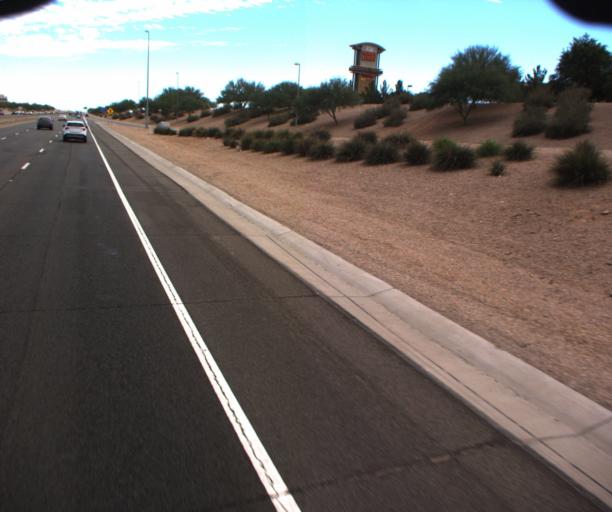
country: US
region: Arizona
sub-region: Maricopa County
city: Chandler
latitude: 33.2828
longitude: -111.7879
